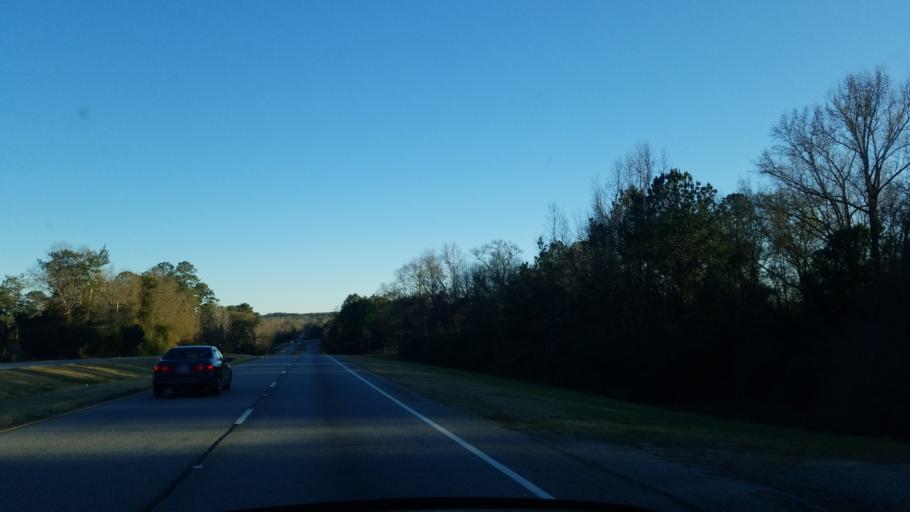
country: US
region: Georgia
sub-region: Chattahoochee County
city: Cusseta
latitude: 32.2877
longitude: -84.7650
